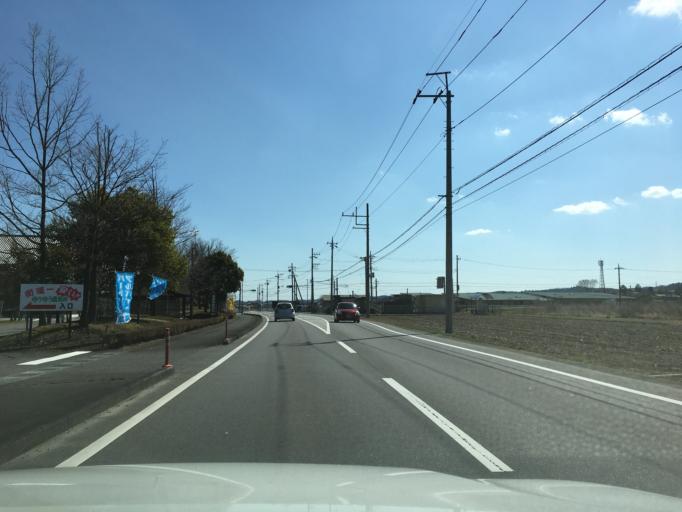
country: JP
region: Tochigi
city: Karasuyama
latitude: 36.7656
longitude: 140.1350
